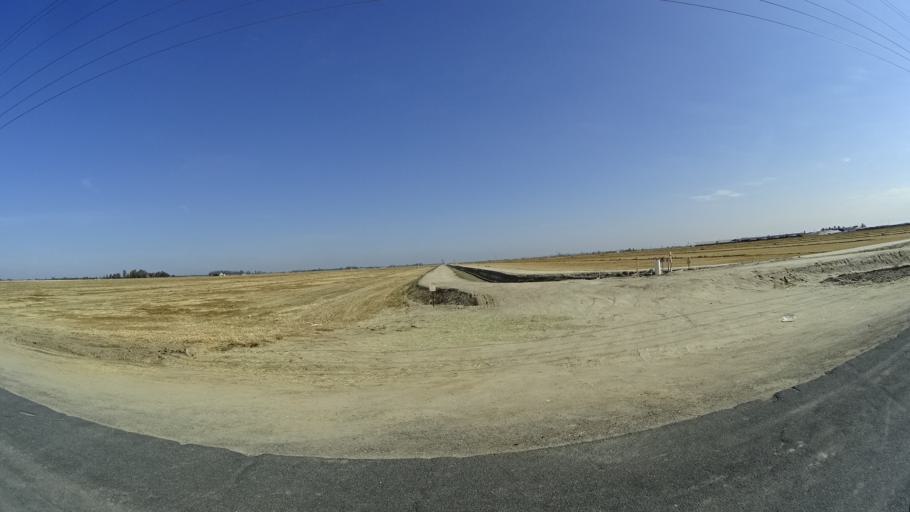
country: US
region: California
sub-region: Kings County
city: Home Garden
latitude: 36.2258
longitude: -119.6640
